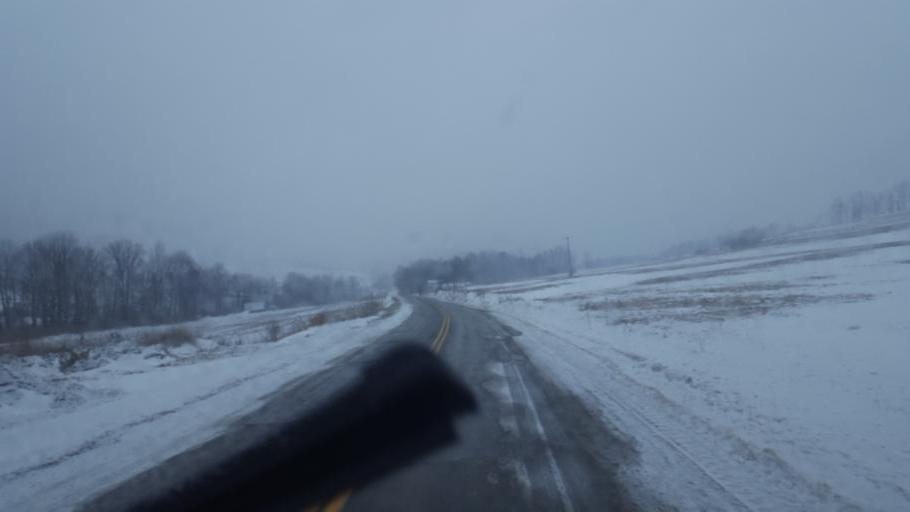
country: US
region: New York
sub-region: Steuben County
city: Canisteo
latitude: 42.1370
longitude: -77.5431
